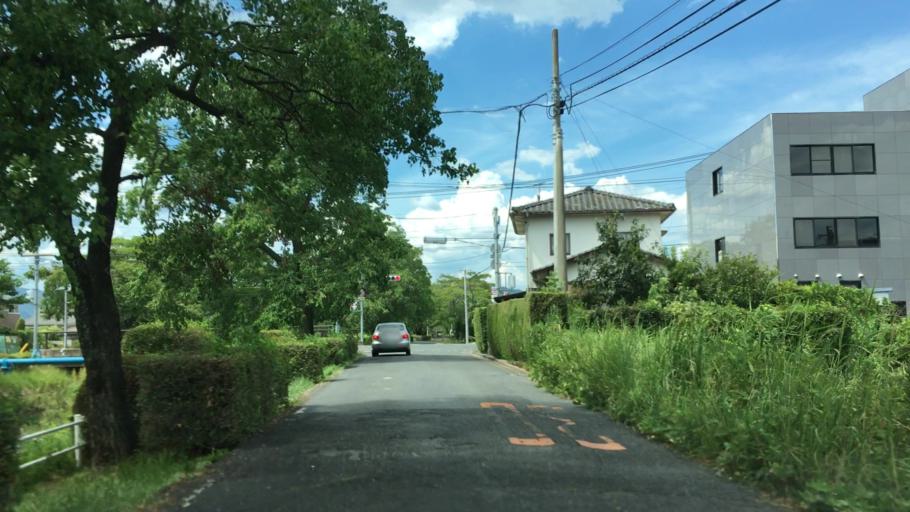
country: JP
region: Saga Prefecture
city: Saga-shi
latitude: 33.2687
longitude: 130.2830
